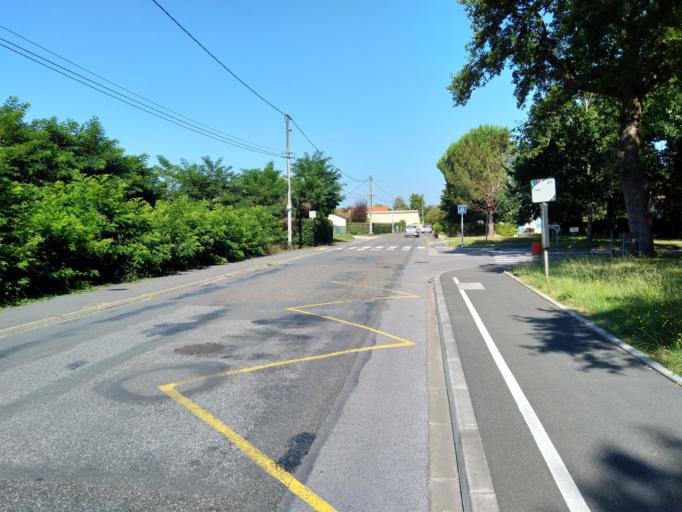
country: FR
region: Aquitaine
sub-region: Departement des Landes
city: Saint-Paul-les-Dax
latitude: 43.7326
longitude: -1.0587
